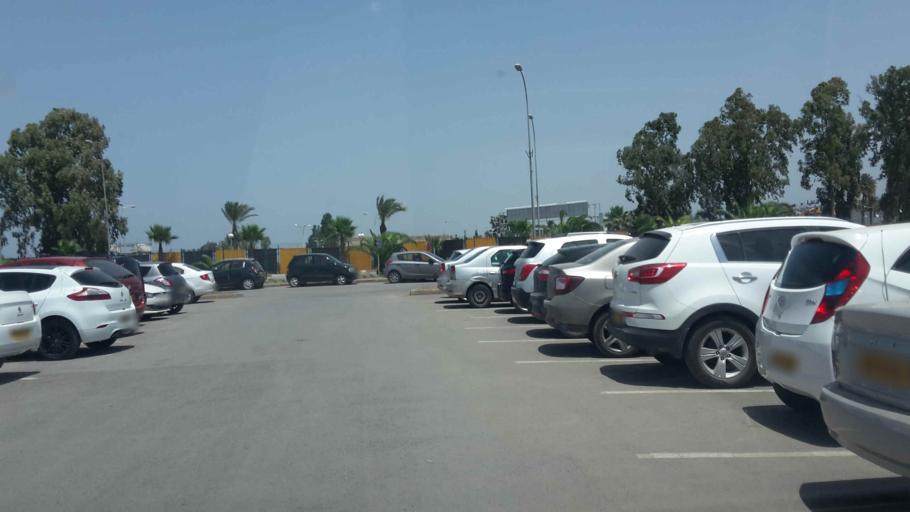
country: DZ
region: Alger
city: Dar el Beida
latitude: 36.7005
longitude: 3.2081
